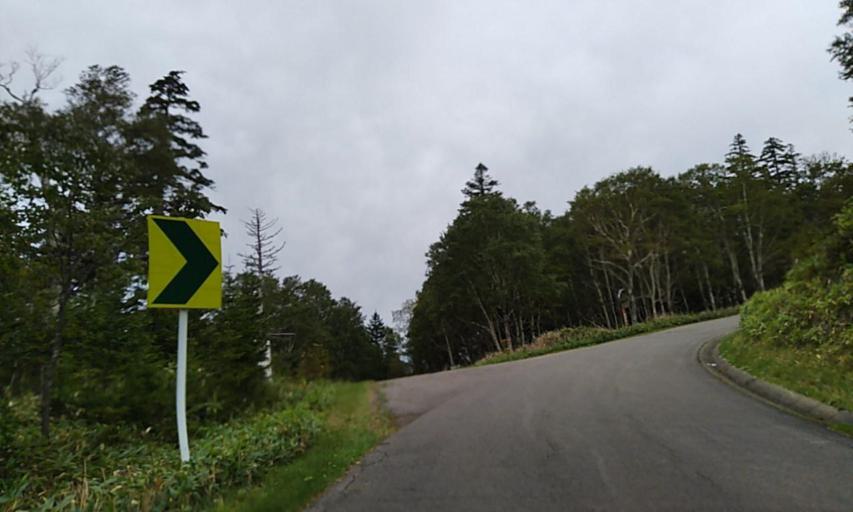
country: JP
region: Hokkaido
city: Bihoro
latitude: 43.5662
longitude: 144.2183
